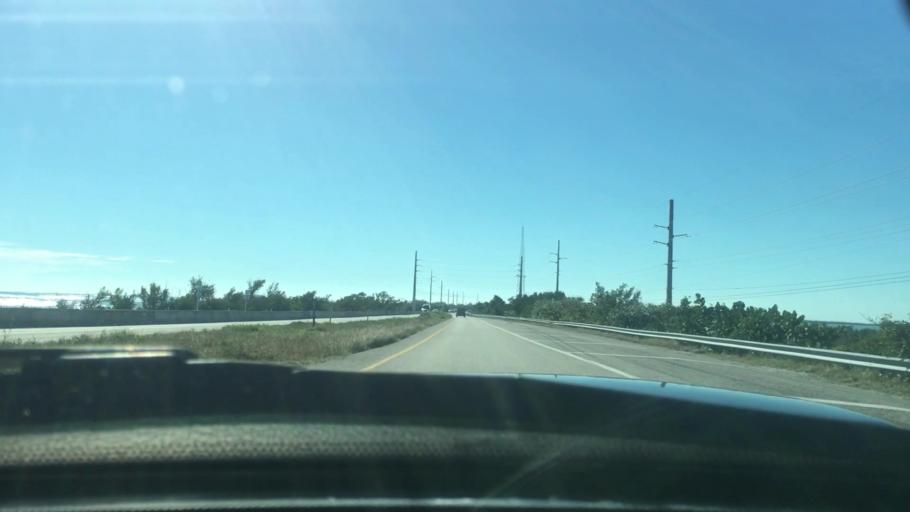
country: US
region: Florida
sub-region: Monroe County
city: Big Pine Key
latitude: 24.6552
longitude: -81.3001
